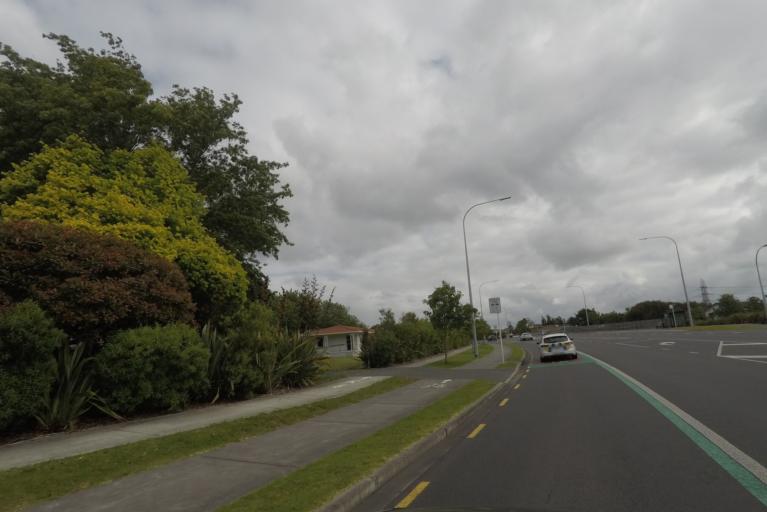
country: NZ
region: Auckland
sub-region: Auckland
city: Rothesay Bay
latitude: -36.7345
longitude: 174.6916
